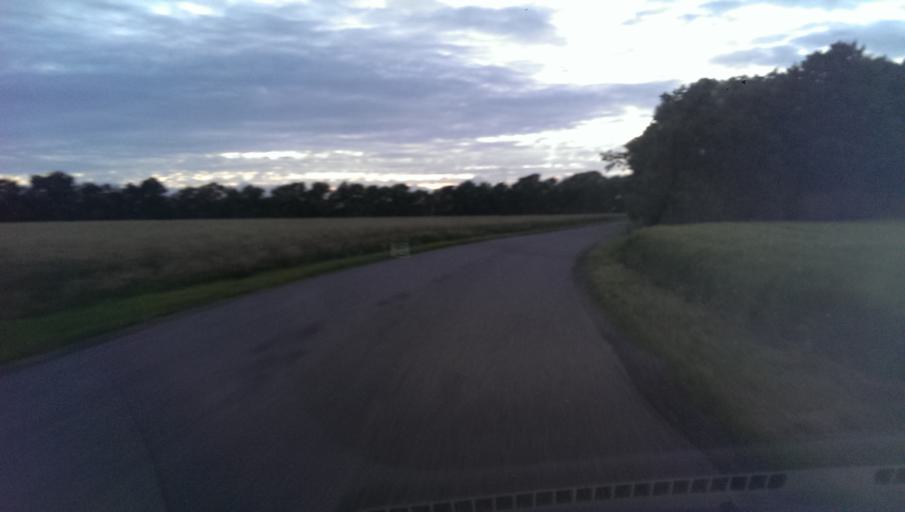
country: DK
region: South Denmark
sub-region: Esbjerg Kommune
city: Esbjerg
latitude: 55.5285
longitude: 8.4904
